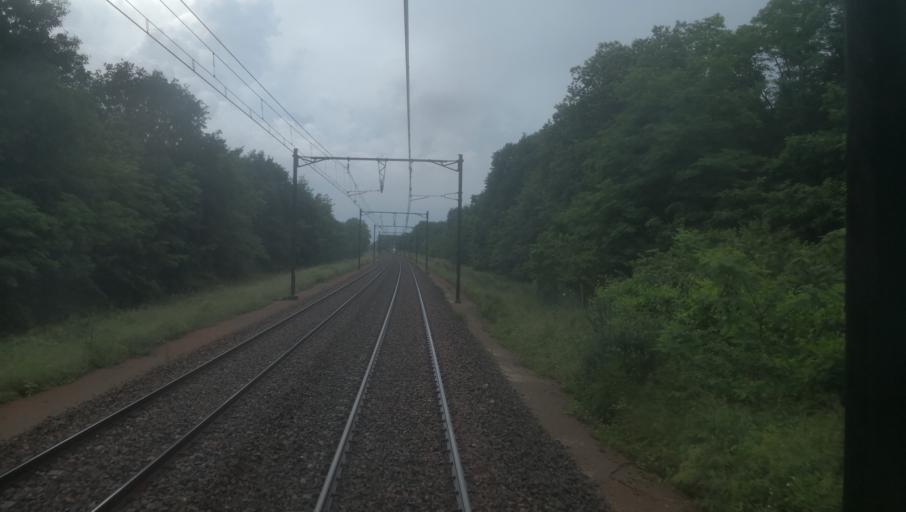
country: FR
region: Centre
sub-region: Departement du Loiret
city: Saint-Cyr-en-Val
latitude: 47.8228
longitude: 1.9484
